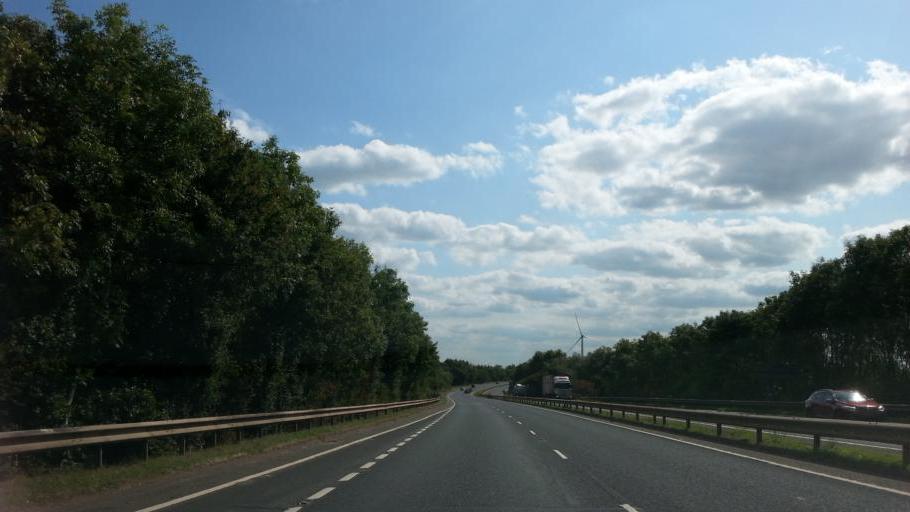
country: GB
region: England
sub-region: Leicestershire
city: Mountsorrel
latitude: 52.7157
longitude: -1.1261
